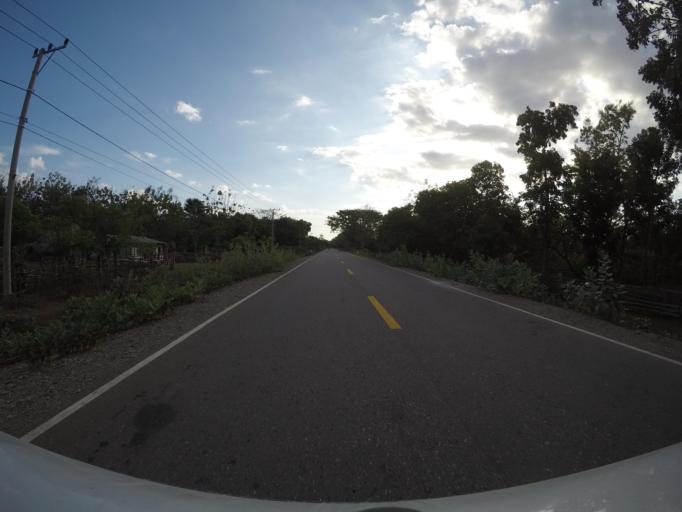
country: TL
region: Bobonaro
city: Maliana
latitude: -8.8932
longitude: 125.0116
